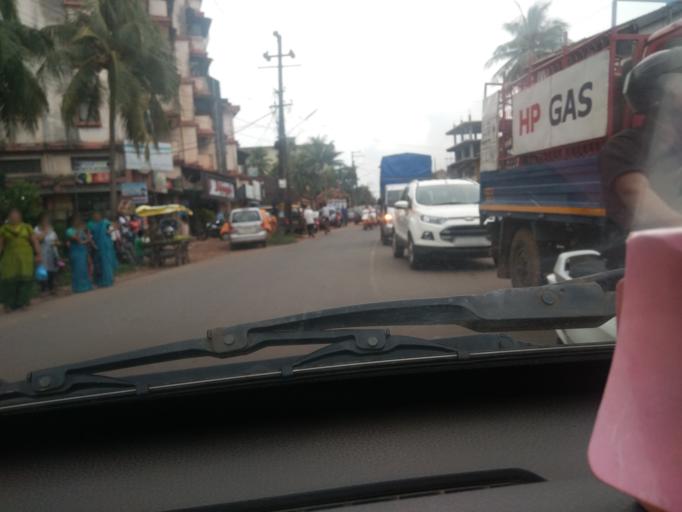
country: IN
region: Goa
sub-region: South Goa
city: Raia
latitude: 15.2906
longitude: 73.9636
